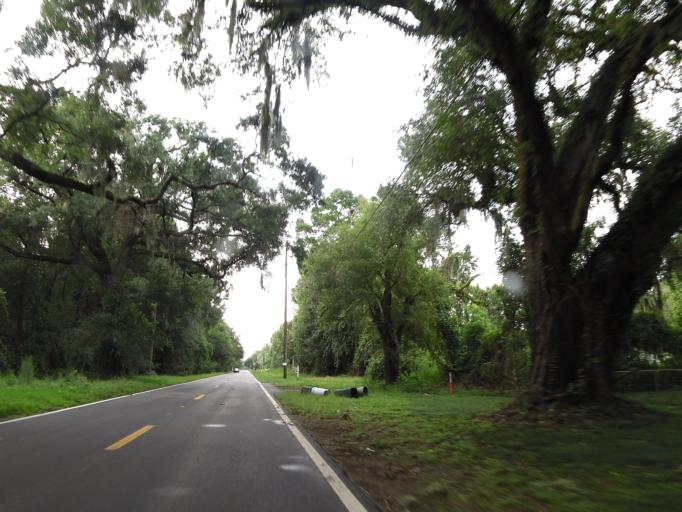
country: US
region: Florida
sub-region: Nassau County
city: Nassau Village-Ratliff
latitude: 30.4087
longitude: -81.7574
